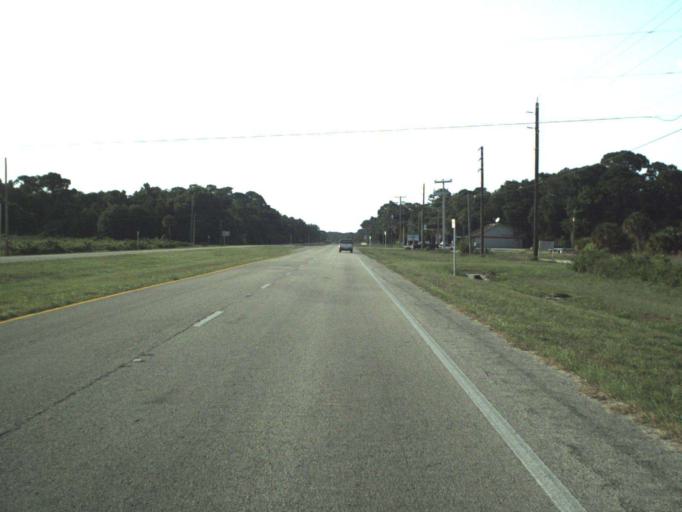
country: US
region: Florida
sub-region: Volusia County
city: Oak Hill
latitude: 28.8986
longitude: -80.8626
